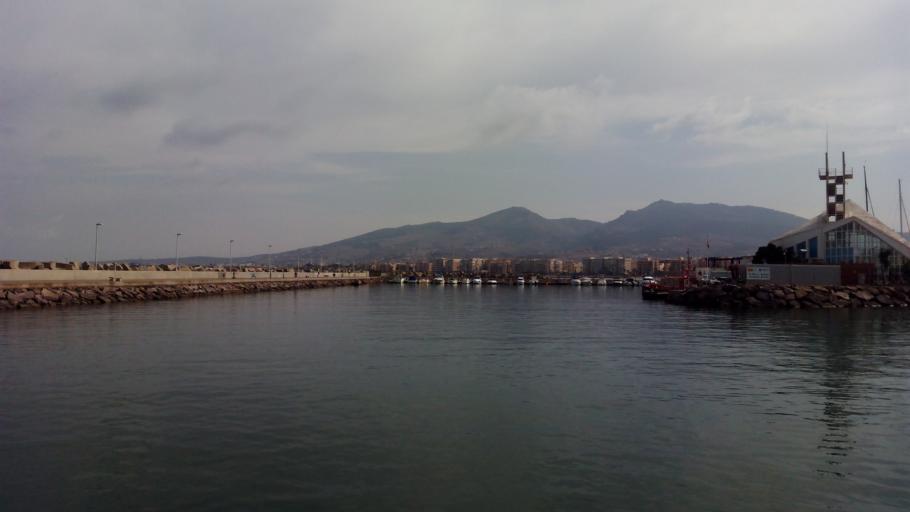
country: ES
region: Melilla
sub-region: Melilla
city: Melilla
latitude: 35.2892
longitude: -2.9324
